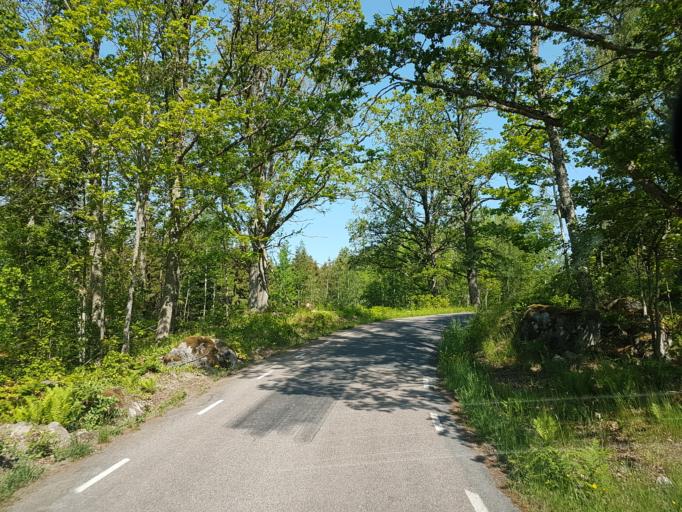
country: SE
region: OEstergoetland
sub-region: Atvidabergs Kommun
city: Atvidaberg
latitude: 58.2543
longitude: 16.2089
